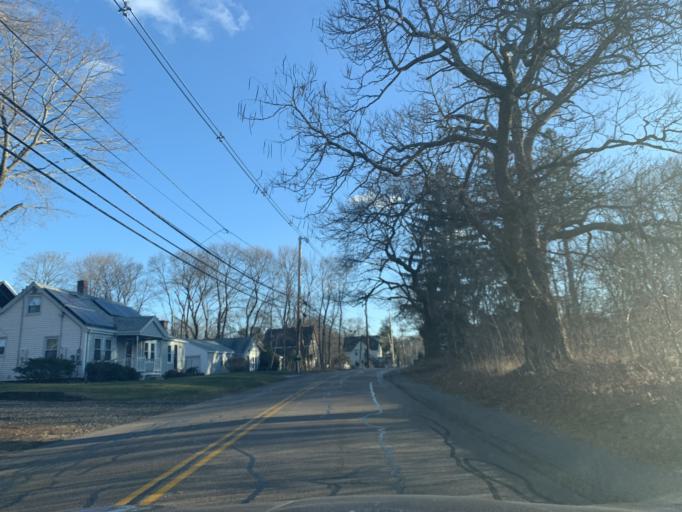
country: US
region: Massachusetts
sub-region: Bristol County
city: Norton
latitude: 41.9444
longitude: -71.2034
